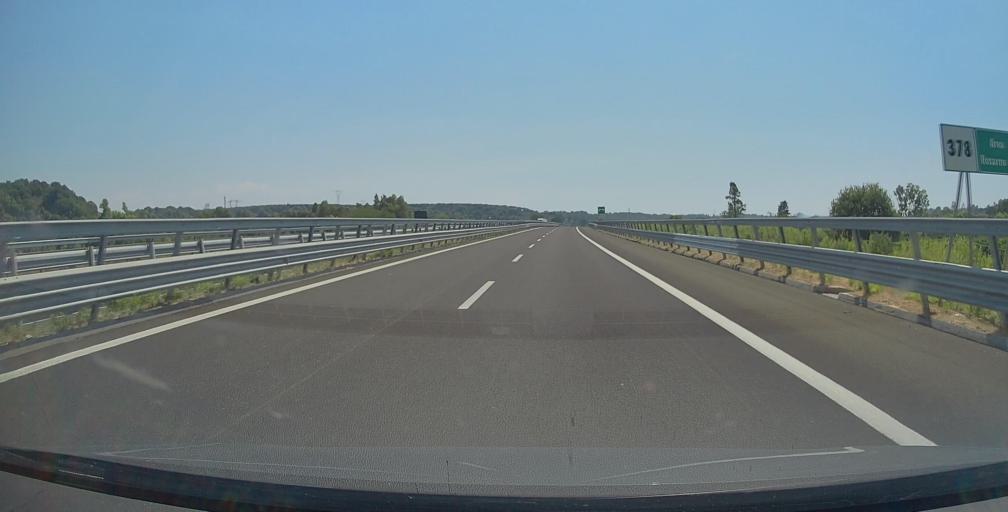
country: IT
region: Calabria
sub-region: Provincia di Reggio Calabria
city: Candidoni
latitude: 38.5099
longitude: 16.0446
